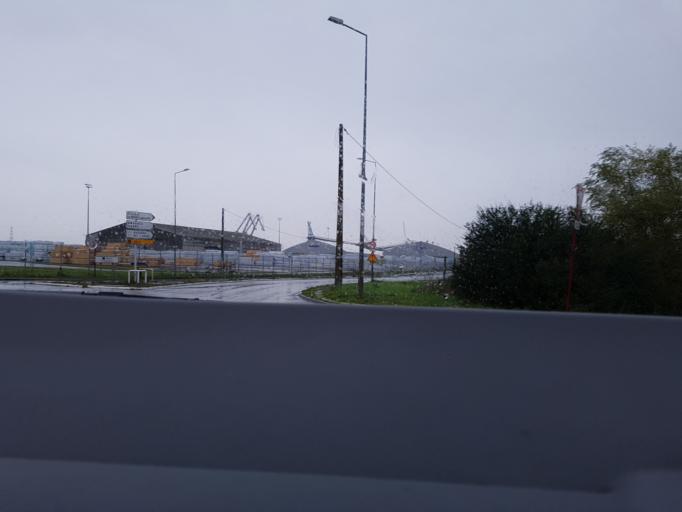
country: FR
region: Aquitaine
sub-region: Departement de la Gironde
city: Bassens
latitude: 44.8935
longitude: -0.5297
